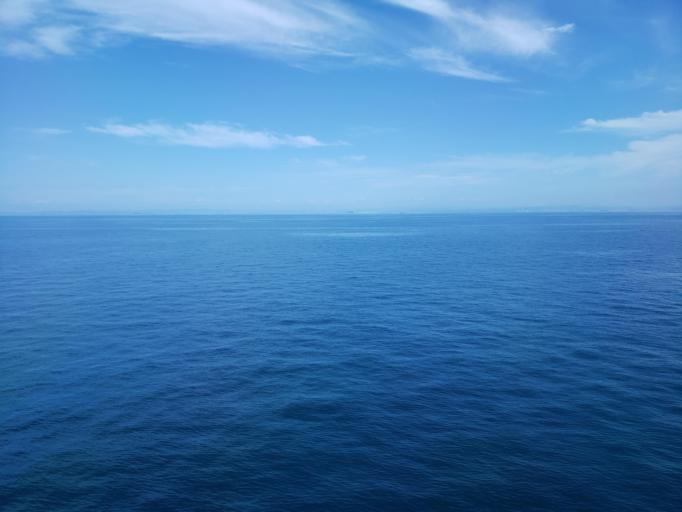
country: JP
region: Hyogo
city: Kakogawacho-honmachi
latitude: 34.5581
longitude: 134.7609
